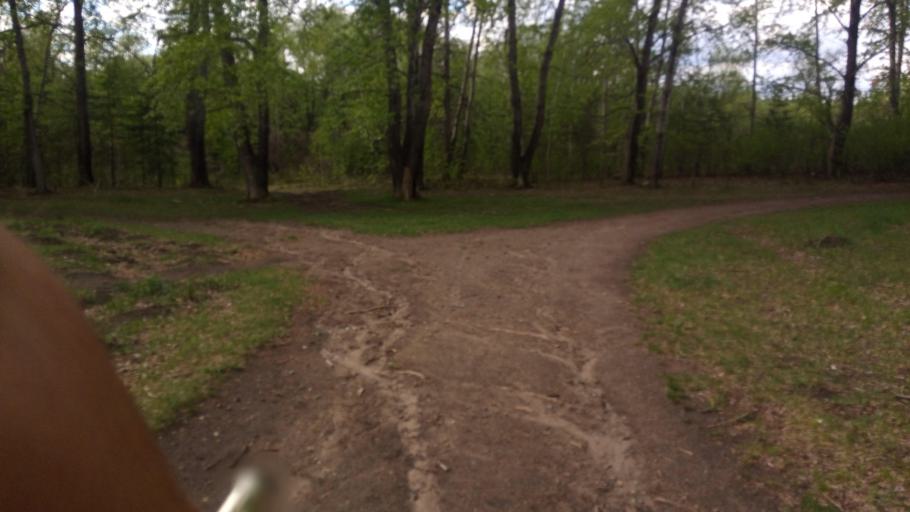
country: RU
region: Chelyabinsk
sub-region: Gorod Chelyabinsk
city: Chelyabinsk
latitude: 55.1679
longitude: 61.3414
